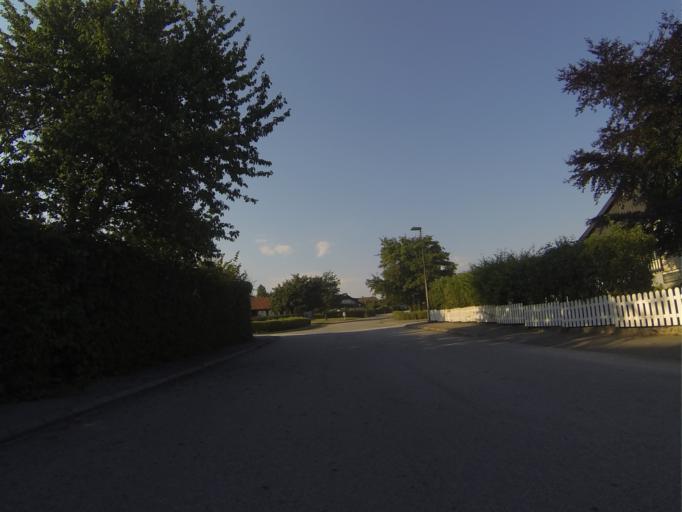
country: SE
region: Skane
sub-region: Lunds Kommun
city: Genarp
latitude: 55.6671
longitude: 13.3568
